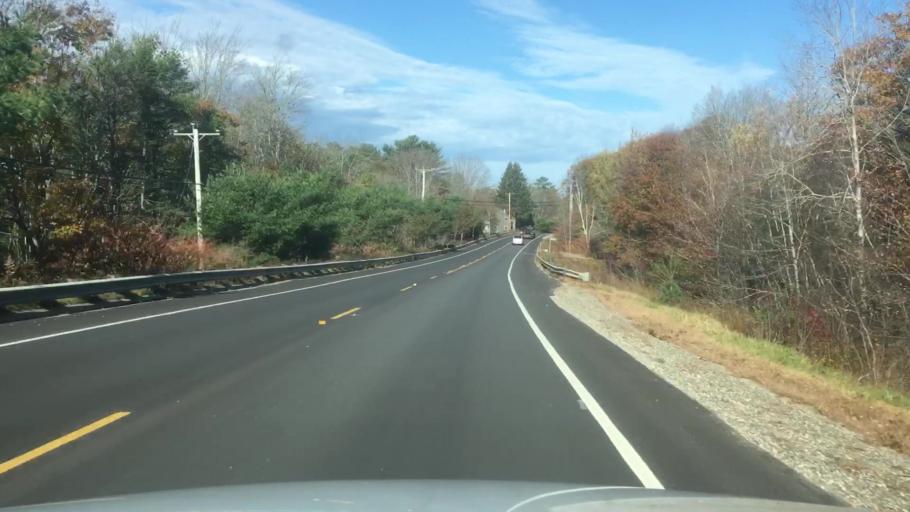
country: US
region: Maine
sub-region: Sagadahoc County
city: Woolwich
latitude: 43.8909
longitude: -69.7913
